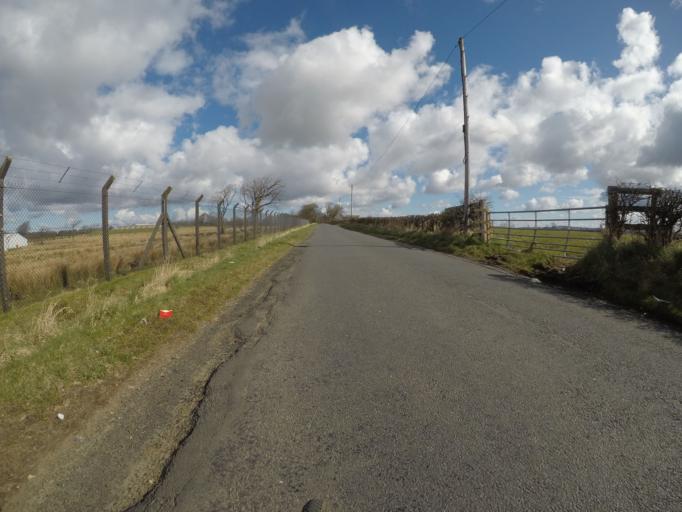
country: GB
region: Scotland
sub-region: North Ayrshire
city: Beith
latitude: 55.7255
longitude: -4.6089
